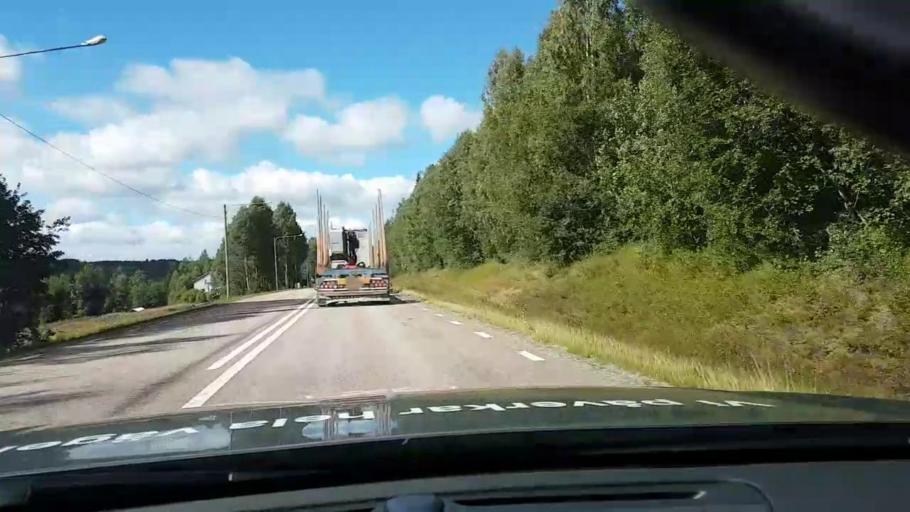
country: SE
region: Vaesternorrland
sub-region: OErnskoeldsviks Kommun
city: Bjasta
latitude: 63.3834
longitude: 18.3988
